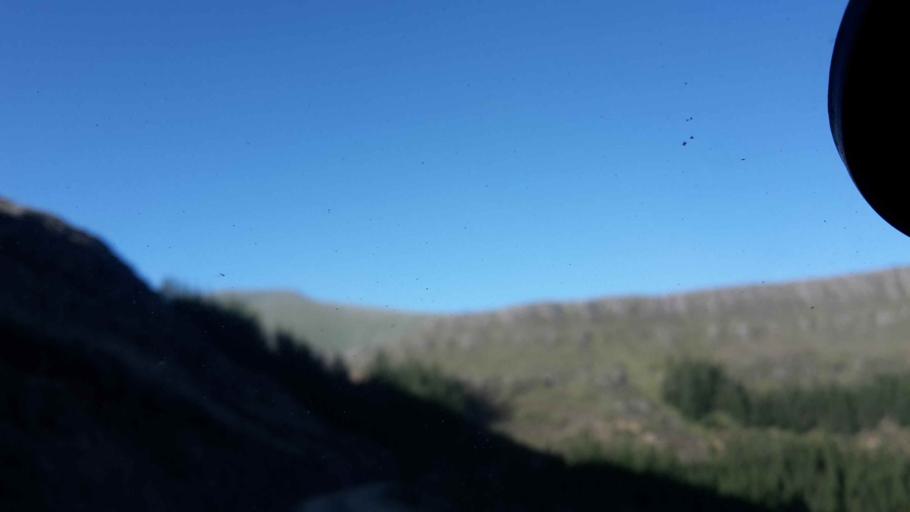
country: BO
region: Cochabamba
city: Arani
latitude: -17.7314
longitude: -65.6273
